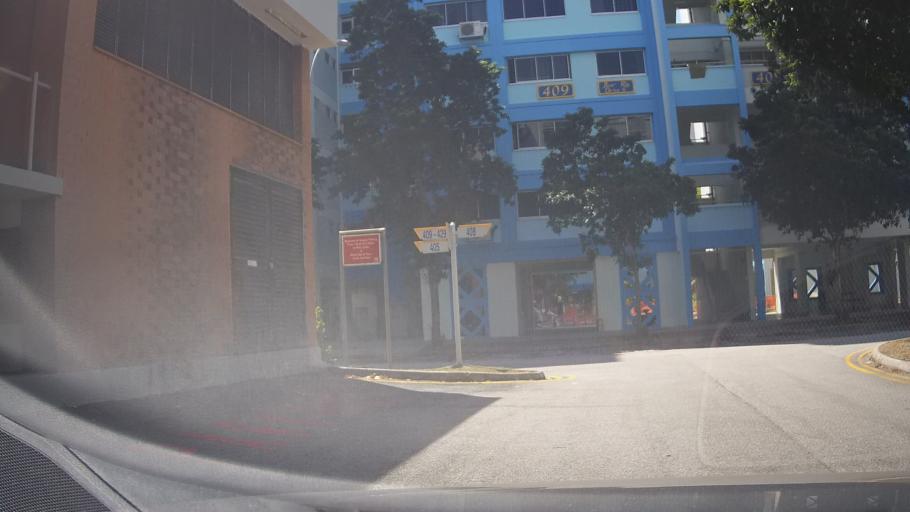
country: MY
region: Johor
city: Kampung Pasir Gudang Baru
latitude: 1.3738
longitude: 103.9541
